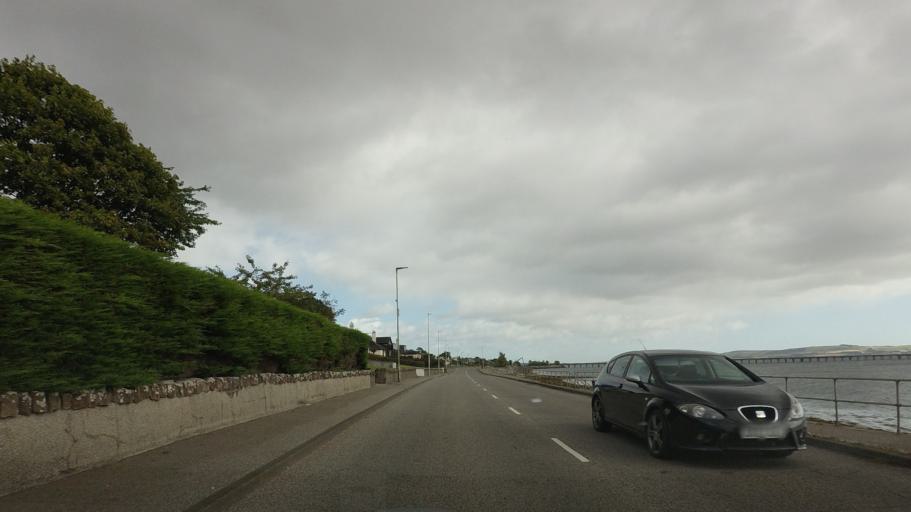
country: GB
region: Scotland
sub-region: Highland
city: Invergordon
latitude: 57.6917
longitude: -4.1563
